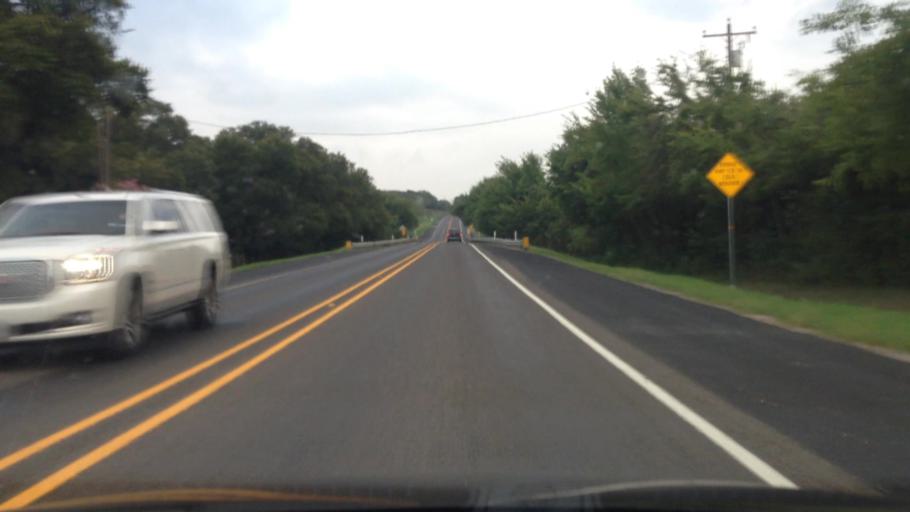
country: US
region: Texas
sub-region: Johnson County
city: Burleson
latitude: 32.5008
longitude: -97.3410
